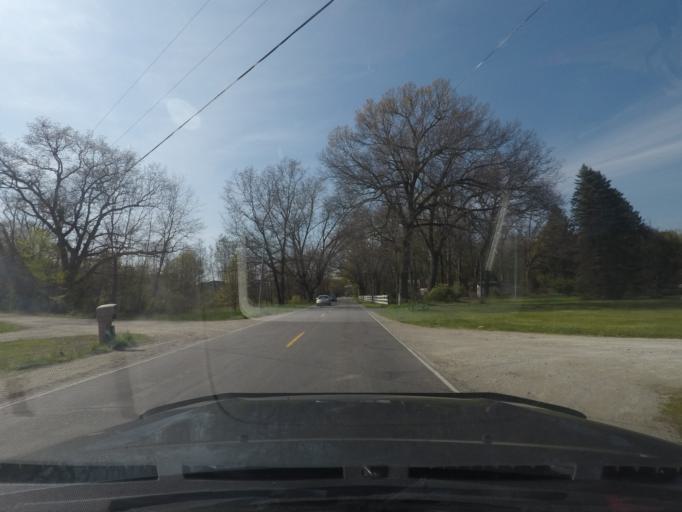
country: US
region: Indiana
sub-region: Elkhart County
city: Elkhart
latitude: 41.7175
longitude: -86.0327
